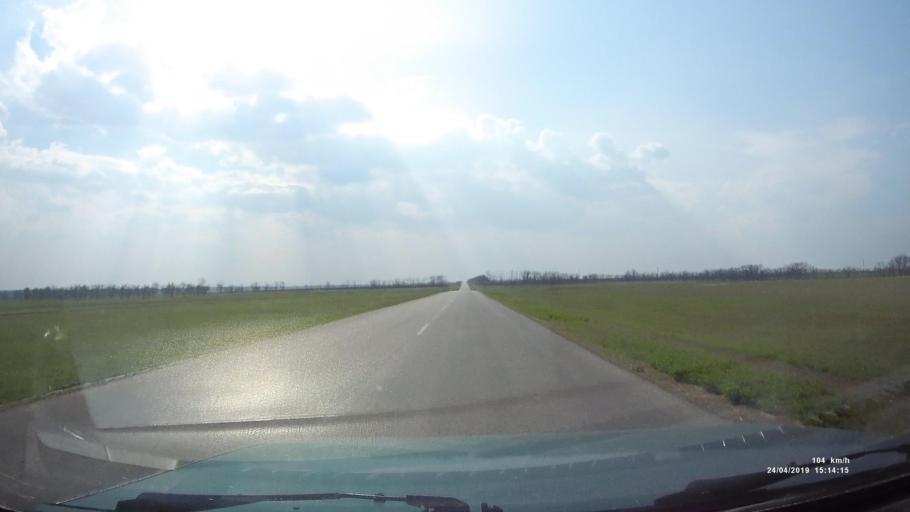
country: RU
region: Rostov
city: Remontnoye
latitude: 46.5462
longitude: 43.2624
